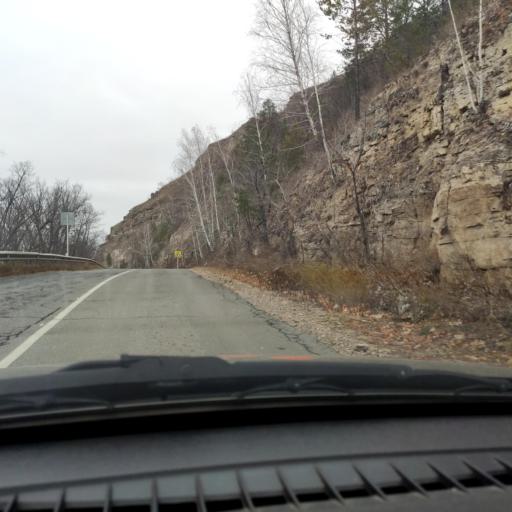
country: RU
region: Samara
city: Povolzhskiy
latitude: 53.4340
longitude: 49.6710
